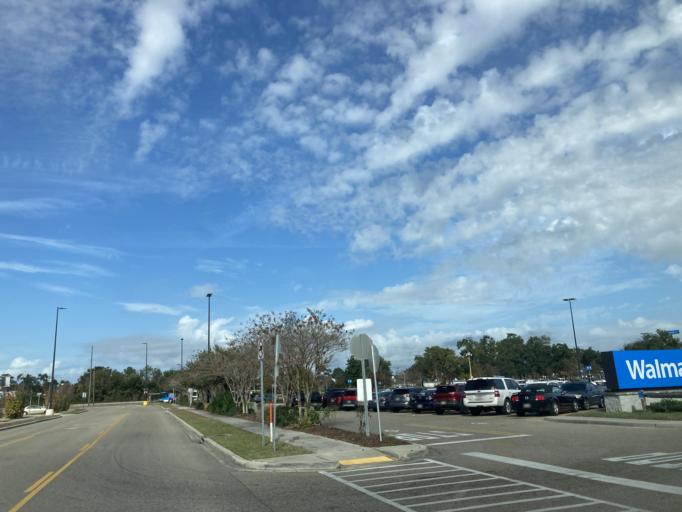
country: US
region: Mississippi
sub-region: Harrison County
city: West Gulfport
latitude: 30.3930
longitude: -88.9960
